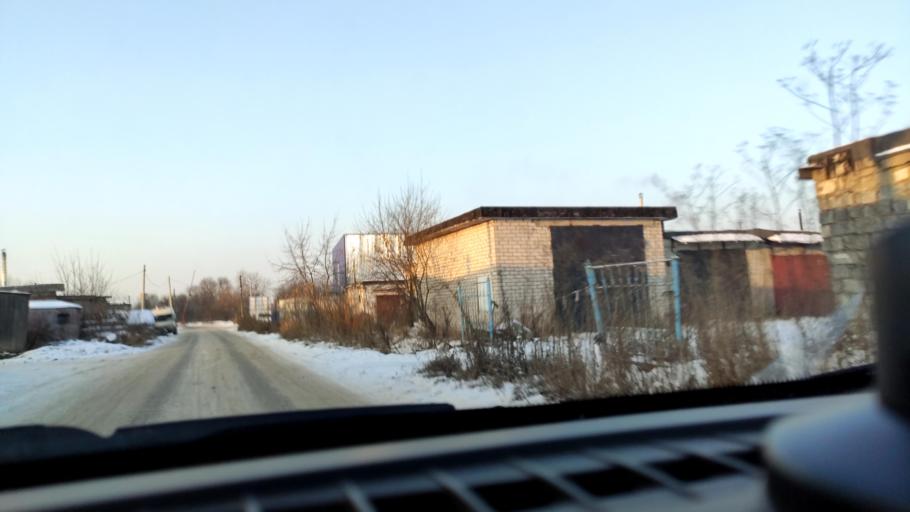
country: RU
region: Perm
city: Kondratovo
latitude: 57.9492
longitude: 56.1852
